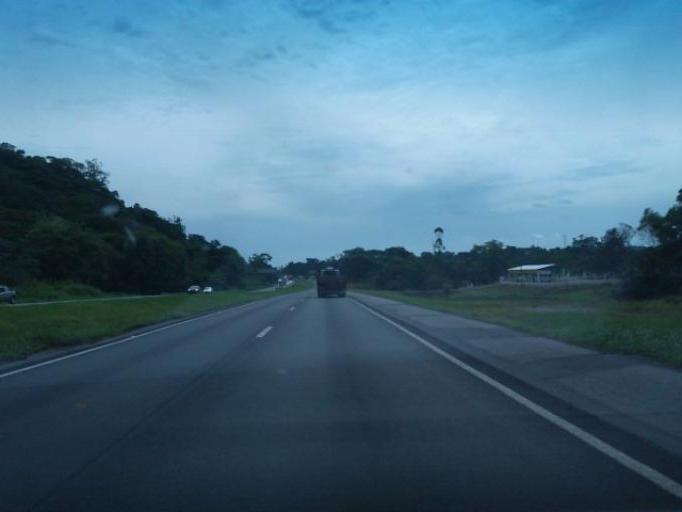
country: BR
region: Sao Paulo
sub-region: Miracatu
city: Miracatu
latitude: -24.2641
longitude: -47.3839
